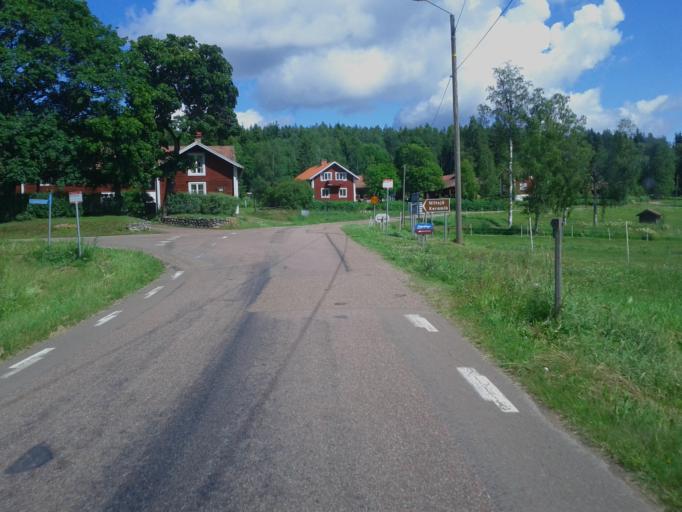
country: SE
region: Dalarna
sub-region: Rattviks Kommun
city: Raettvik
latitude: 60.9173
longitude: 15.0749
